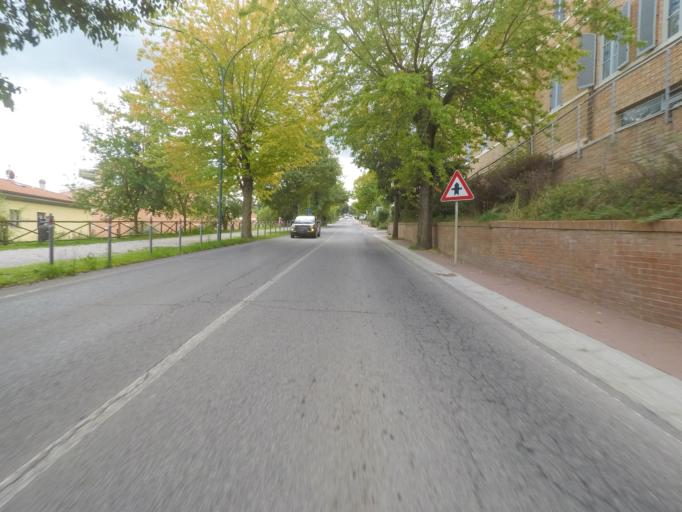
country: IT
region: Tuscany
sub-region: Provincia di Siena
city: Montepulciano
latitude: 43.1019
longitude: 11.7856
